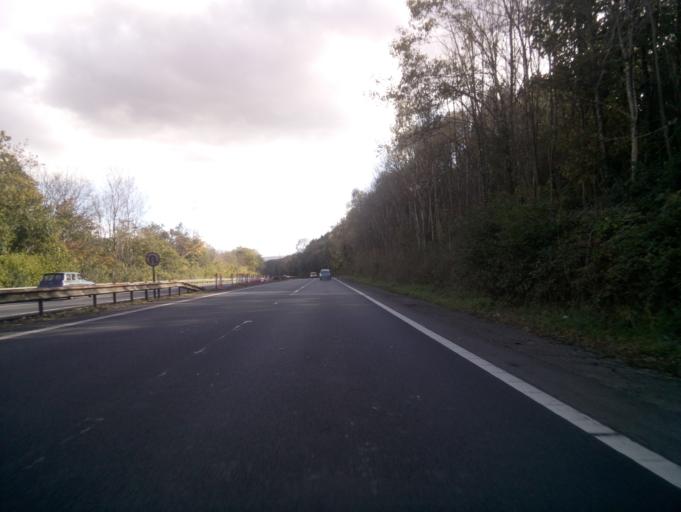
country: GB
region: Wales
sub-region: Merthyr Tydfil County Borough
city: Treharris
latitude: 51.6743
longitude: -3.3359
